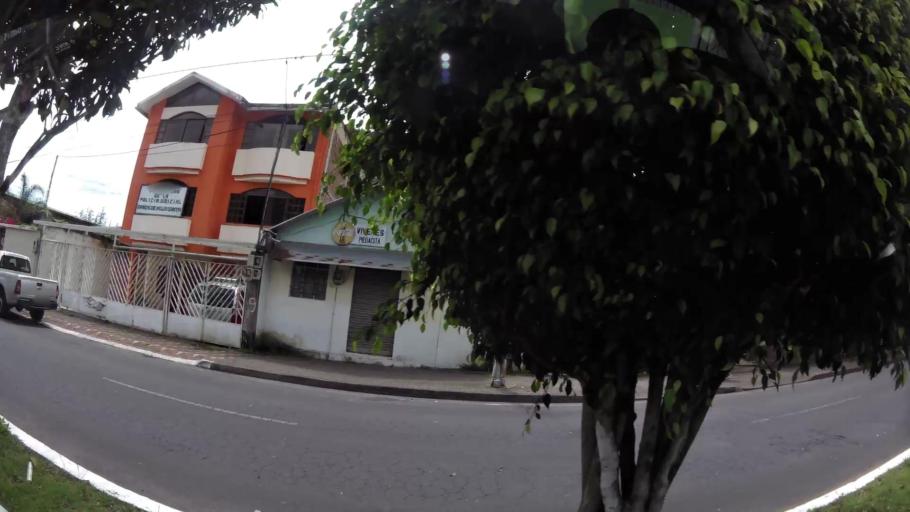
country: EC
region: Tungurahua
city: Banos
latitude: -1.3937
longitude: -78.4193
